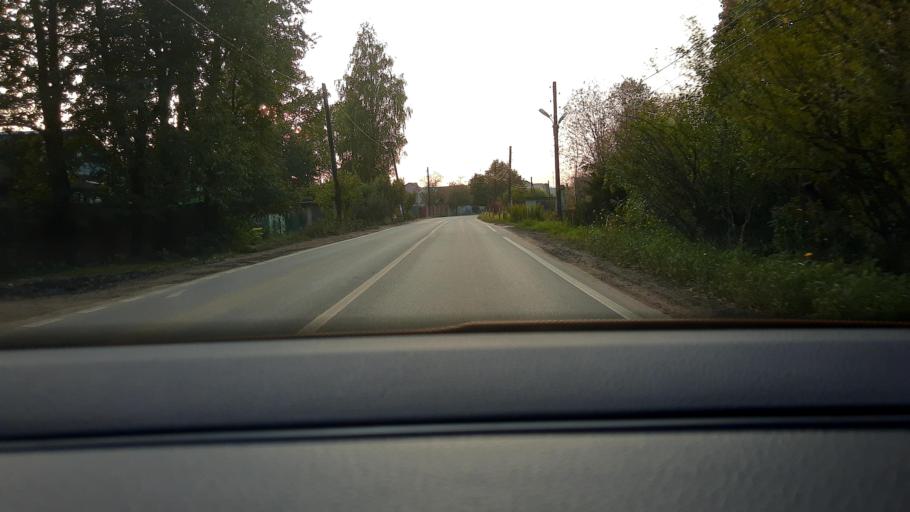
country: RU
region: Moskovskaya
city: Lobnya
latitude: 55.9992
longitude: 37.4195
